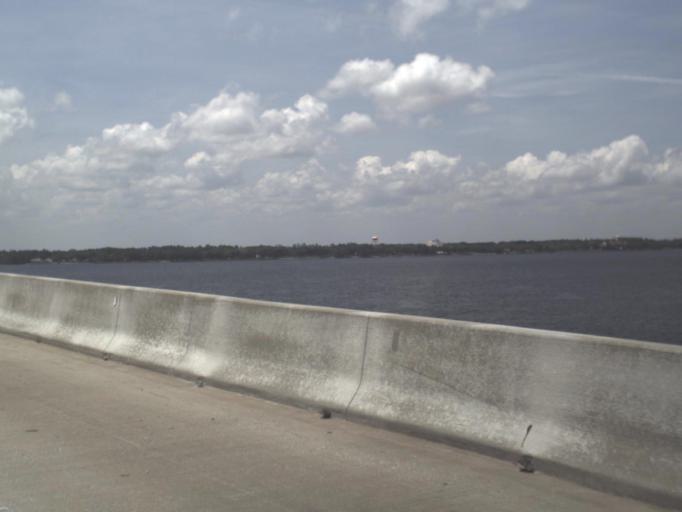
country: US
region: Florida
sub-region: Clay County
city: Orange Park
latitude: 30.1900
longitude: -81.6634
